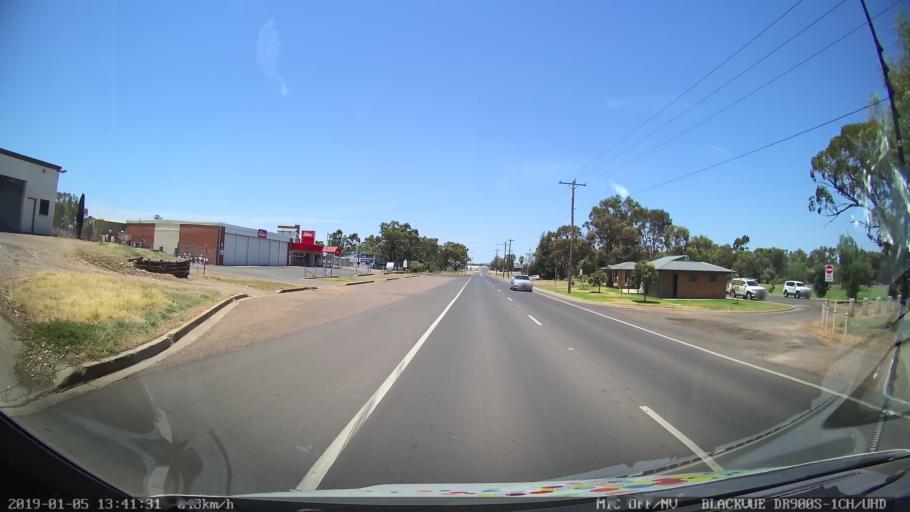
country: AU
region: New South Wales
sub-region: Gunnedah
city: Gunnedah
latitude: -30.9786
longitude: 150.2398
